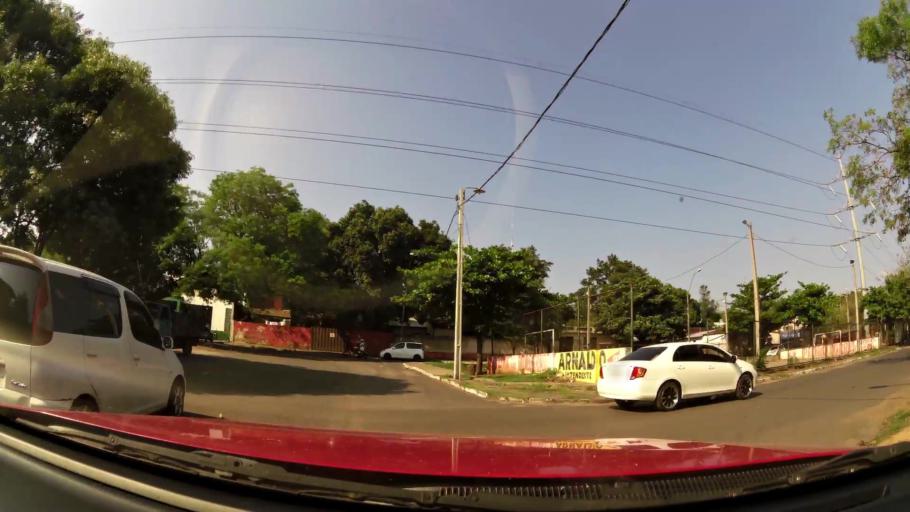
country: PY
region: Asuncion
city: Asuncion
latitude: -25.3121
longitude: -57.6358
